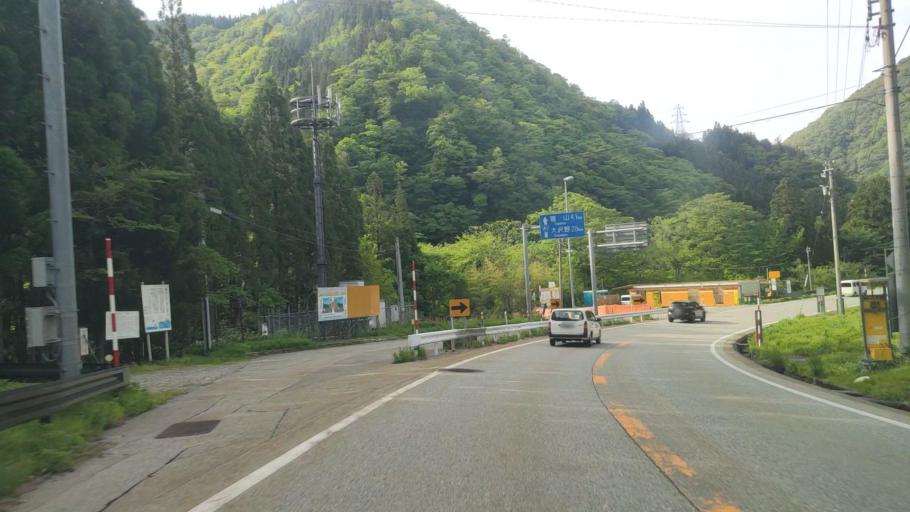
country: JP
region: Toyama
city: Yatsuomachi-higashikumisaka
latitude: 36.3746
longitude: 137.2760
